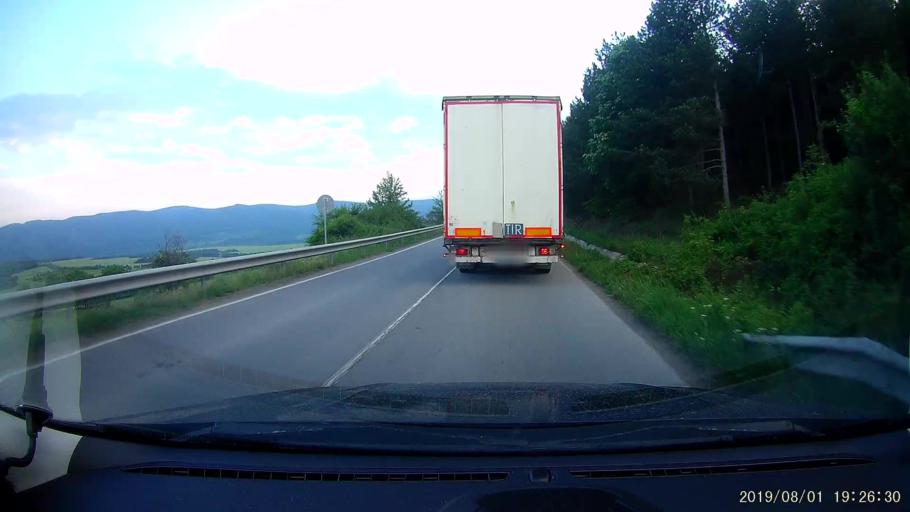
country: BG
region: Burgas
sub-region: Obshtina Sungurlare
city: Sungurlare
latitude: 42.8570
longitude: 26.9402
